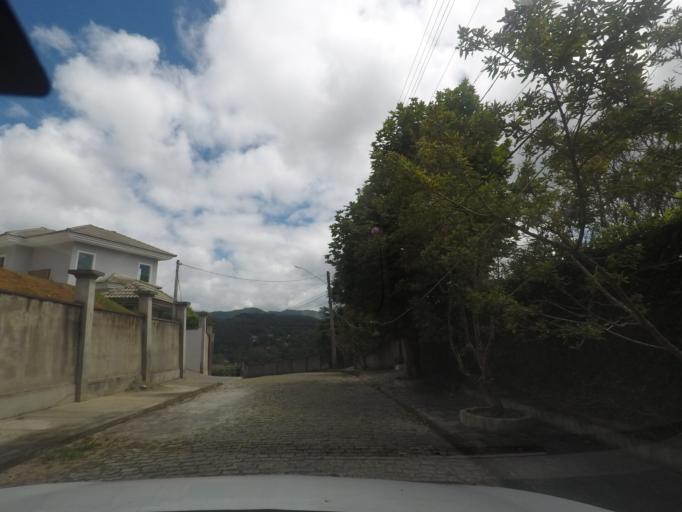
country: BR
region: Rio de Janeiro
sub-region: Teresopolis
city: Teresopolis
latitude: -22.3998
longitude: -42.9848
